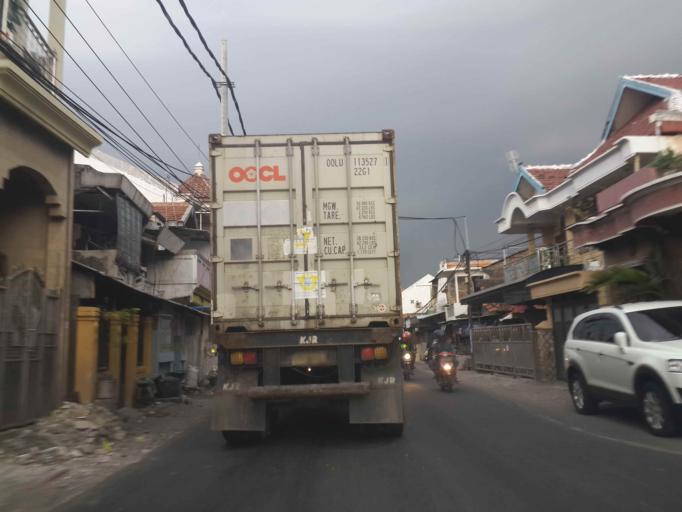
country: ID
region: East Java
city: Kebomas
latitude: -7.2112
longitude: 112.6526
